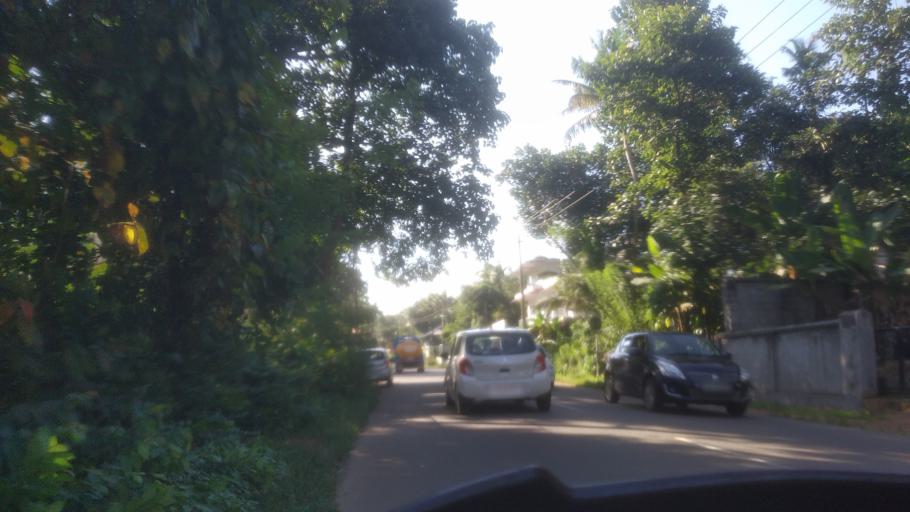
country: IN
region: Kerala
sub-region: Ernakulam
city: Ramamangalam
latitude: 9.9776
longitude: 76.4949
